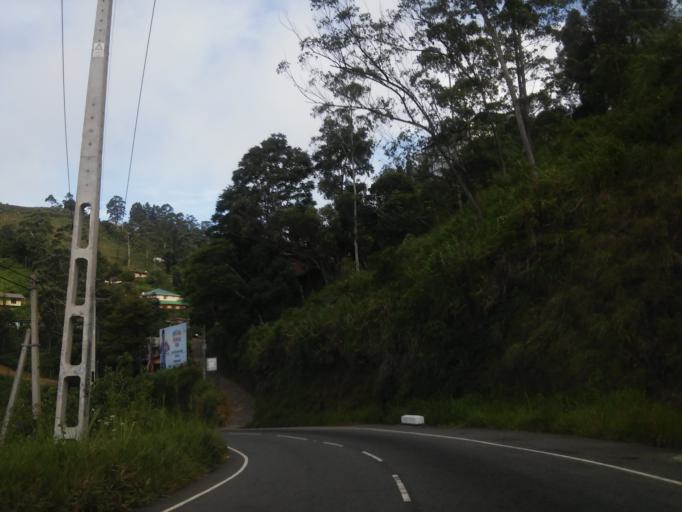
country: LK
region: Uva
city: Haputale
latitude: 6.7652
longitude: 80.9540
